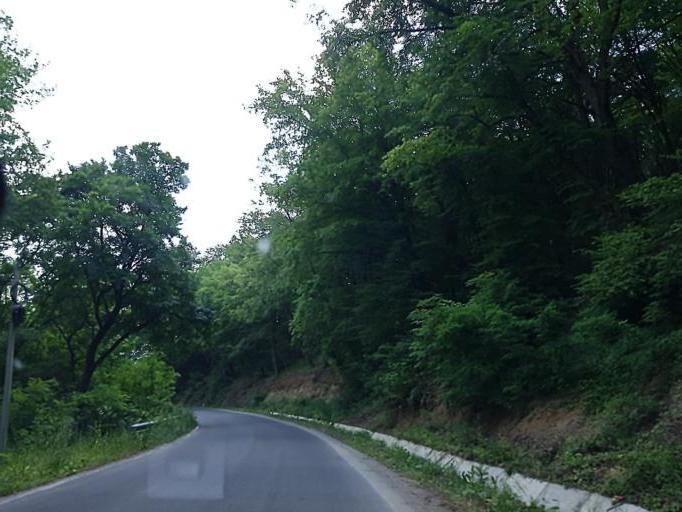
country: RO
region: Sibiu
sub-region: Comuna Seica Mare
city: Seica Mare
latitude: 46.0393
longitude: 24.1588
